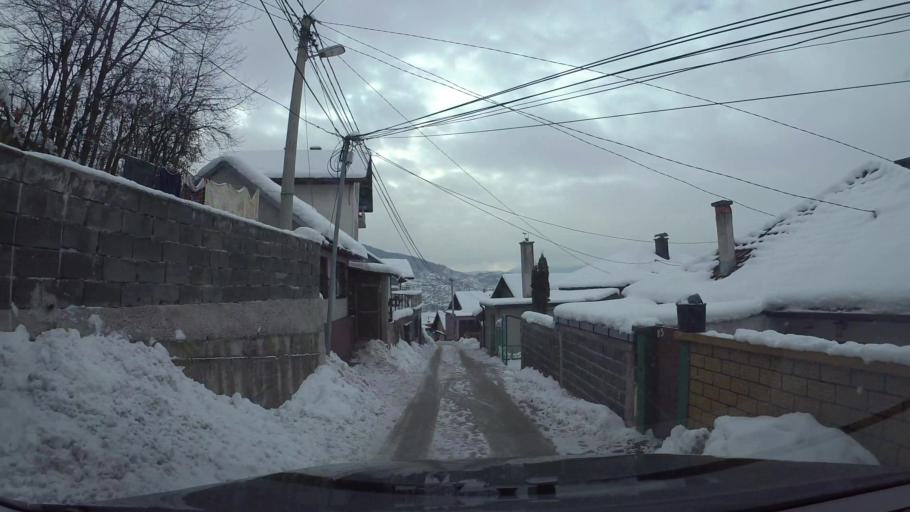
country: BA
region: Federation of Bosnia and Herzegovina
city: Kobilja Glava
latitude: 43.8698
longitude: 18.4378
